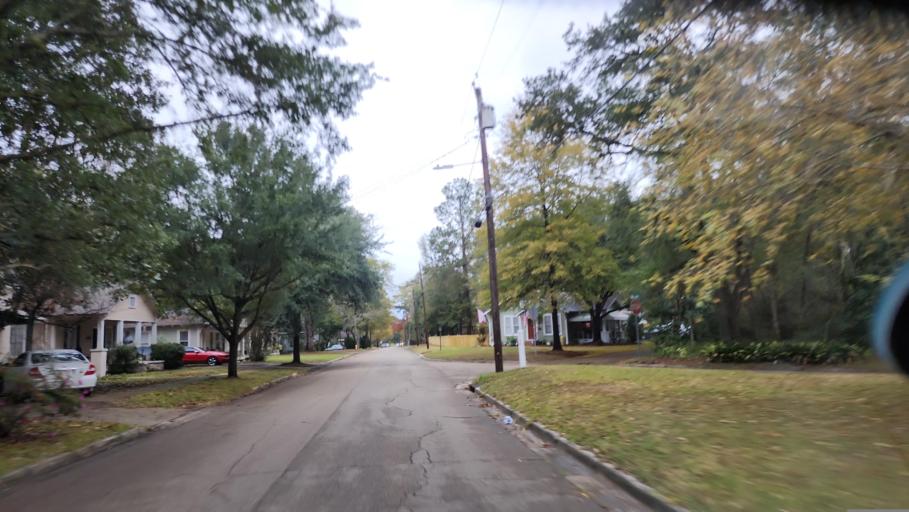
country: US
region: Mississippi
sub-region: Forrest County
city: Hattiesburg
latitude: 31.3203
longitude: -89.3058
